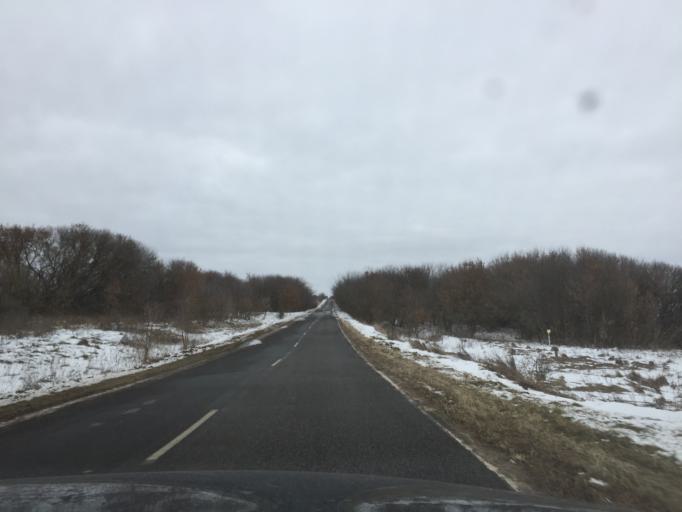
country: RU
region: Tula
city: Teploye
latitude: 53.7943
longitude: 37.6020
